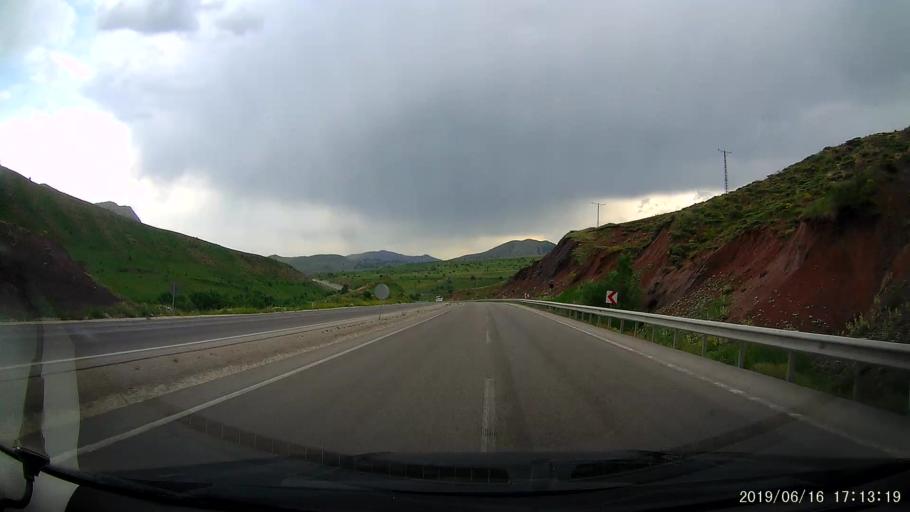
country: TR
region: Erzurum
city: Askale
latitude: 39.8597
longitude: 40.6009
